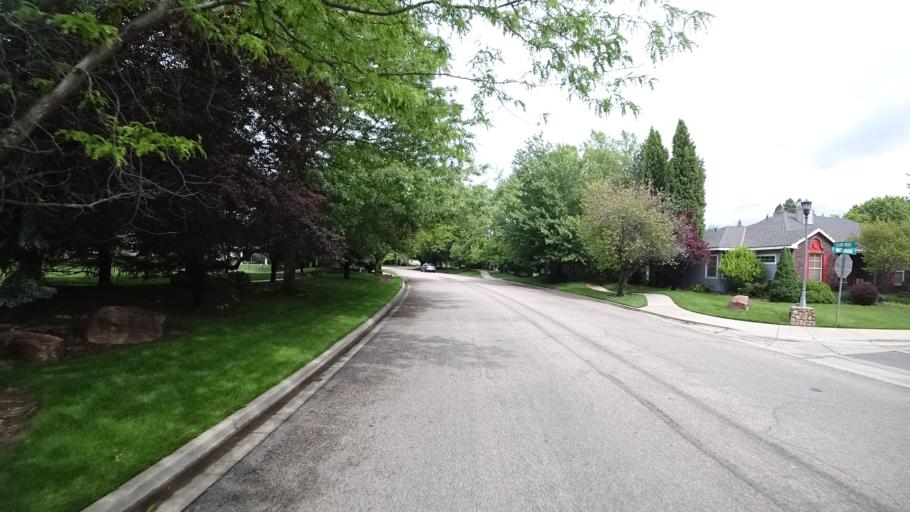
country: US
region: Idaho
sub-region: Ada County
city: Eagle
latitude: 43.6825
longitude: -116.3497
